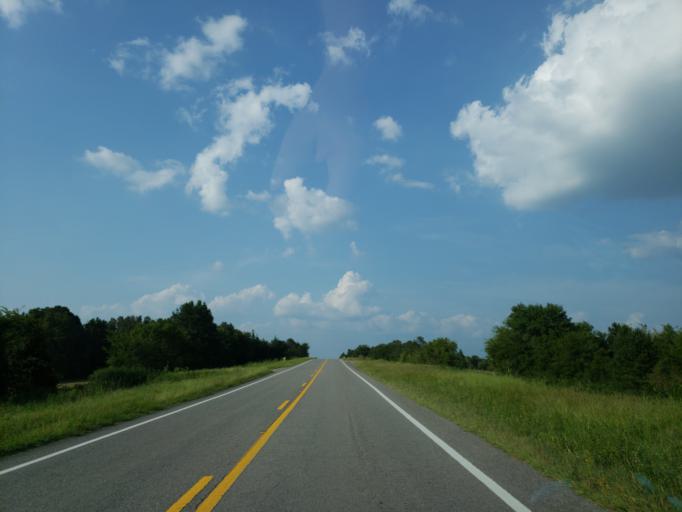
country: US
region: Alabama
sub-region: Greene County
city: Eutaw
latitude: 32.7843
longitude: -87.9770
